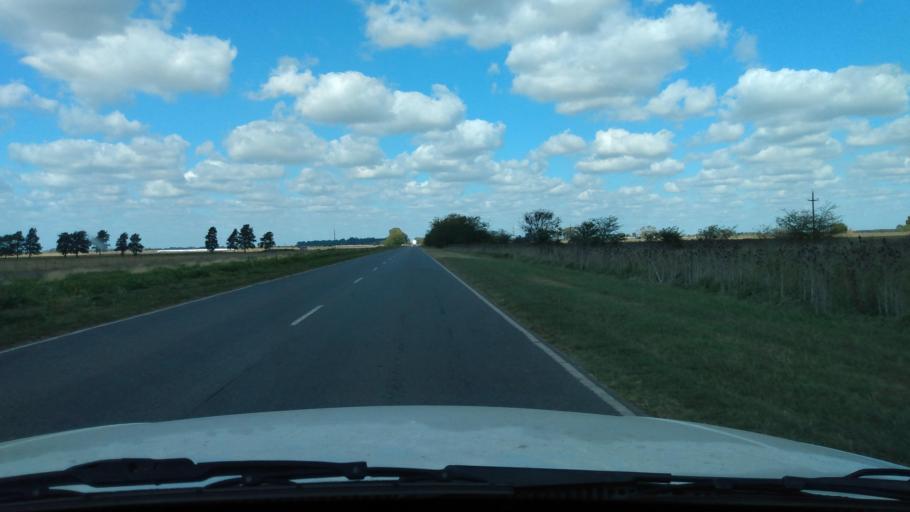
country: AR
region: Buenos Aires
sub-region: Partido de Navarro
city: Navarro
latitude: -34.9677
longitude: -59.3177
